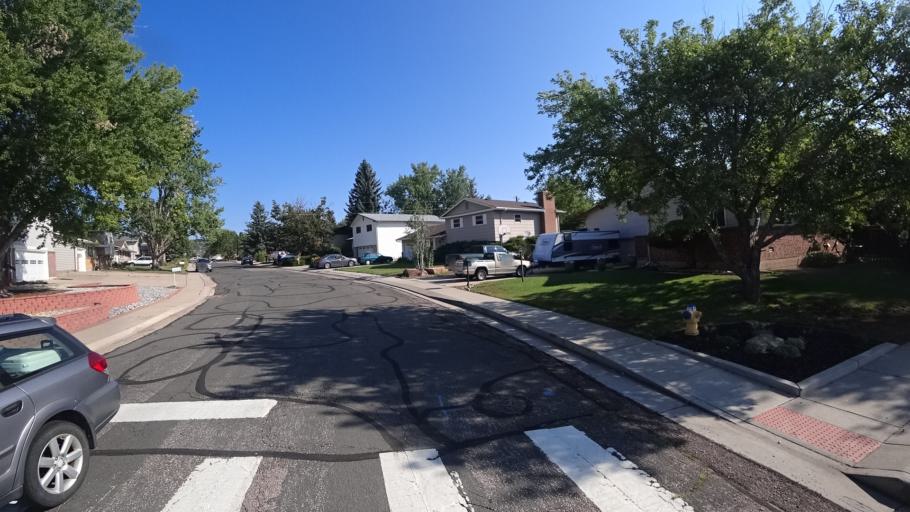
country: US
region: Colorado
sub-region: El Paso County
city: Colorado Springs
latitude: 38.8933
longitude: -104.8395
